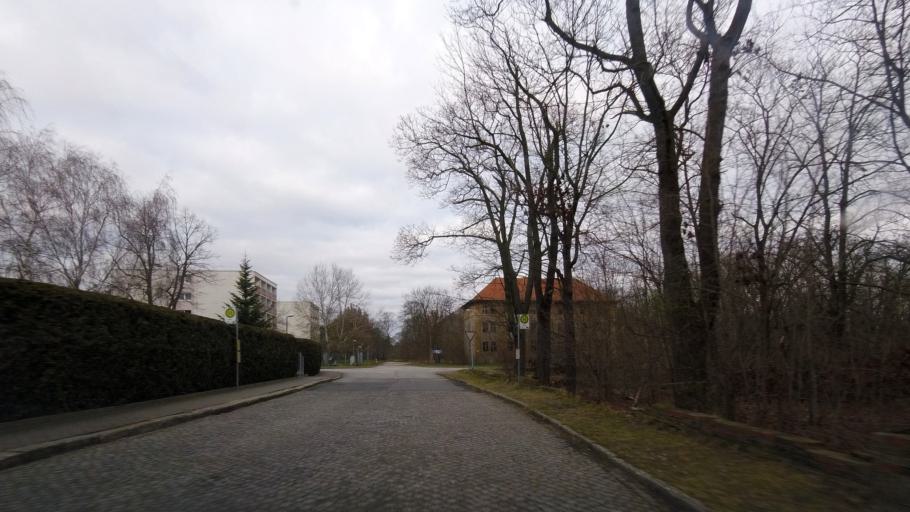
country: DE
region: Brandenburg
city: Juterbog
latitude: 52.0017
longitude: 13.0553
